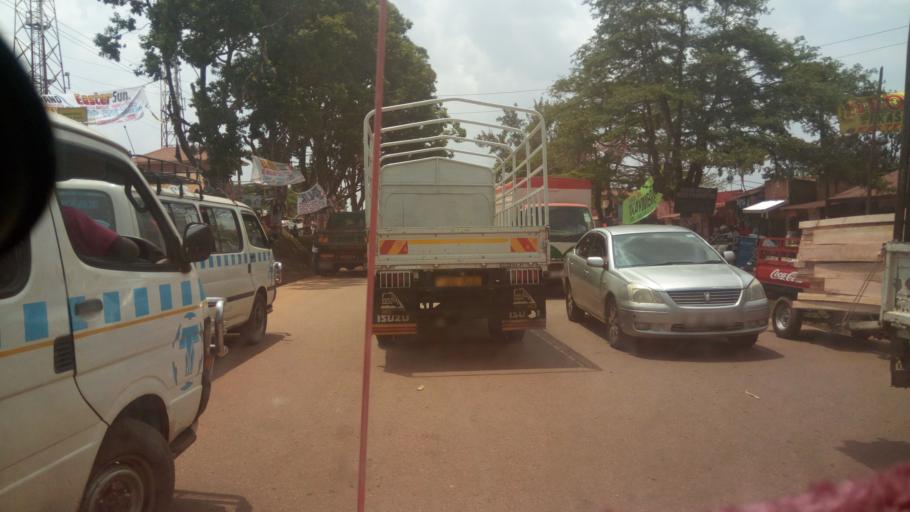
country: UG
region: Central Region
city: Kampala Central Division
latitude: 0.3679
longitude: 32.5233
